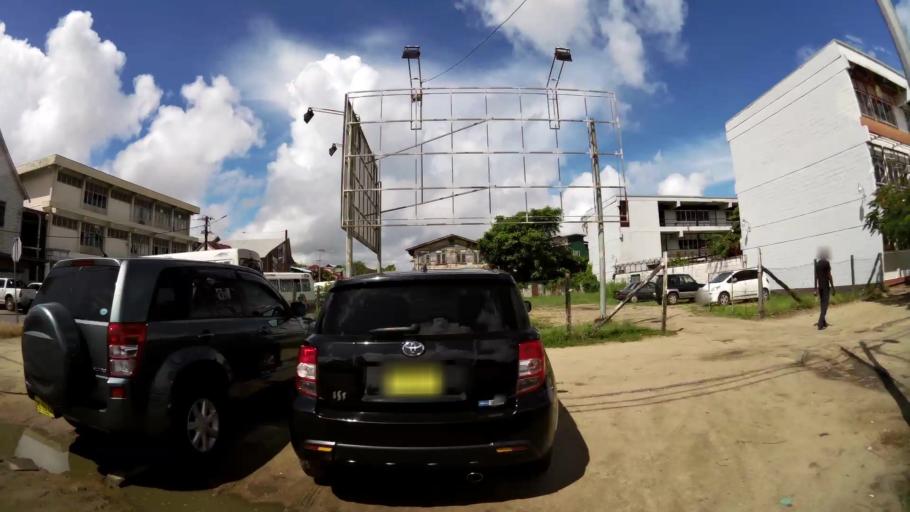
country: SR
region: Paramaribo
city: Paramaribo
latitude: 5.8272
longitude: -55.1634
